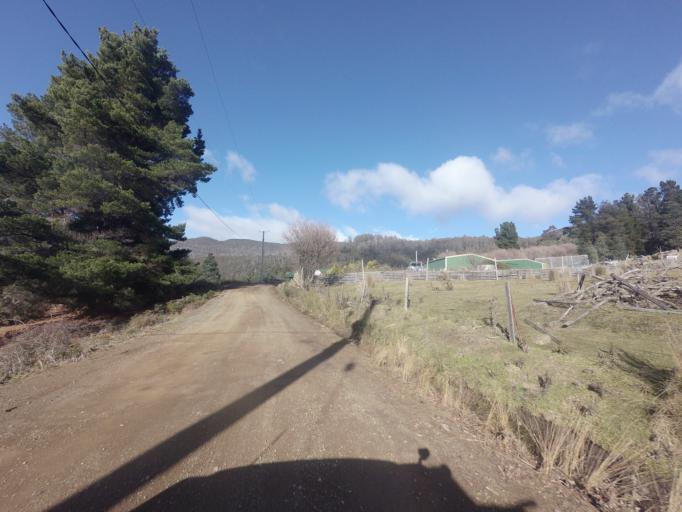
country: AU
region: Tasmania
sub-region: Glenorchy
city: Berriedale
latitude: -42.8555
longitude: 147.1673
